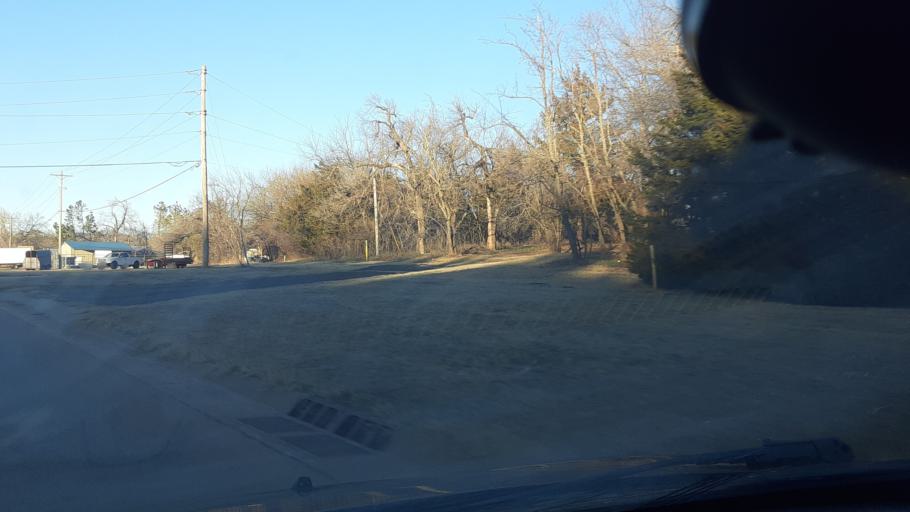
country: US
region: Oklahoma
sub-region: Logan County
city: Guthrie
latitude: 35.8351
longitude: -97.4254
